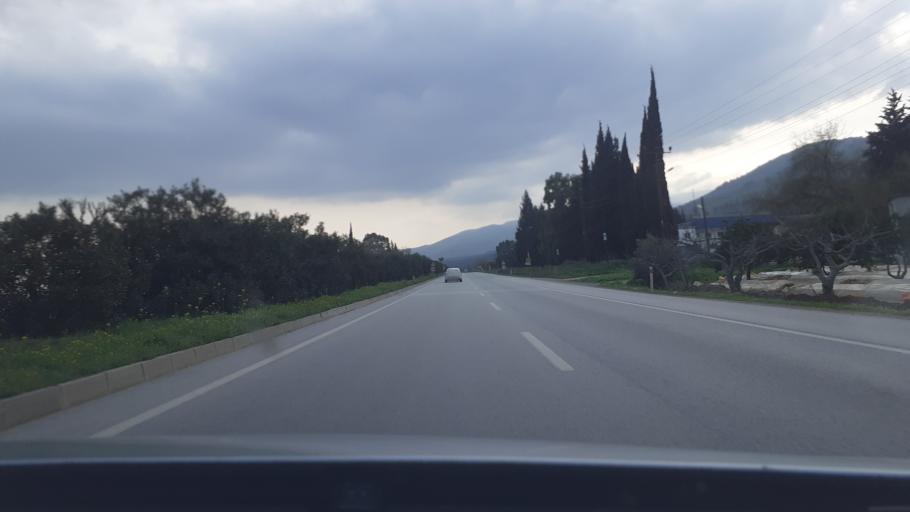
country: TR
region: Hatay
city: Serinyol
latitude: 36.3987
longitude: 36.2431
